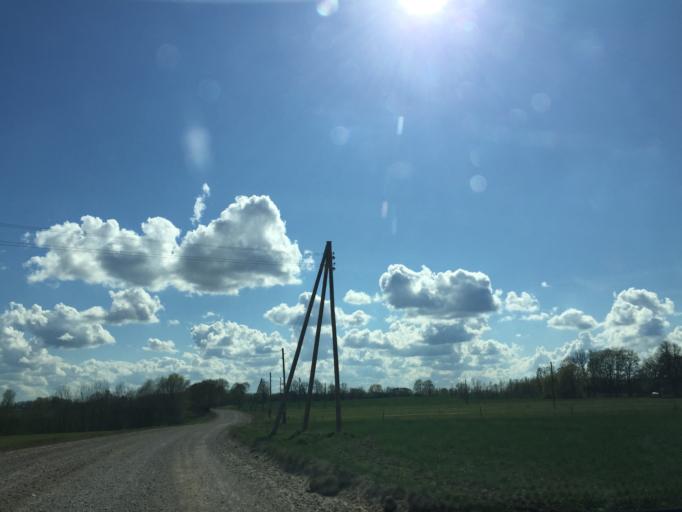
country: LV
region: Strenci
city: Strenci
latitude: 57.4927
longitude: 25.6411
